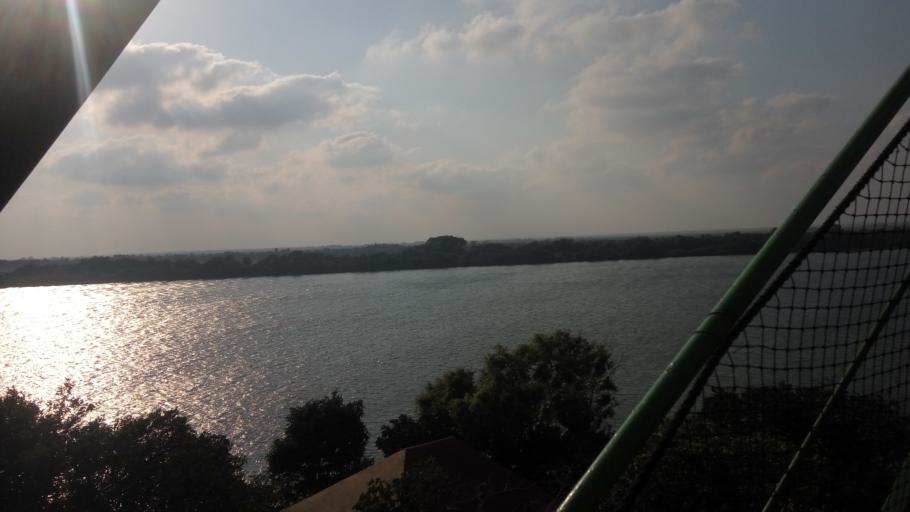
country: MX
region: Tabasco
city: Frontera
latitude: 18.4056
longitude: -92.6479
